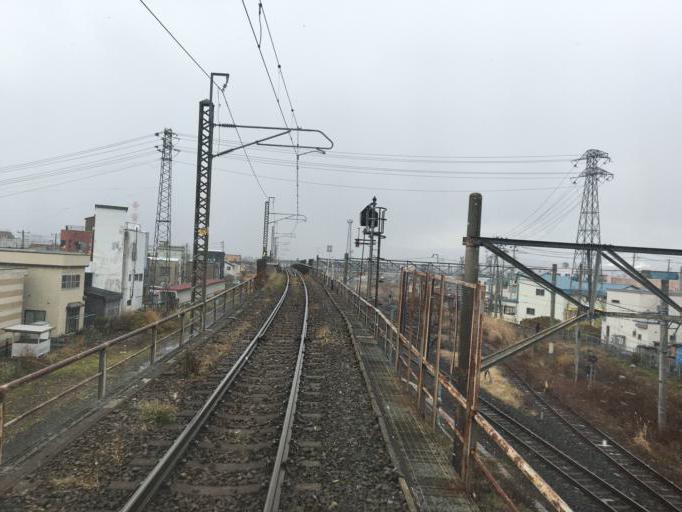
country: JP
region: Aomori
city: Aomori Shi
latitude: 40.8207
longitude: 140.7343
